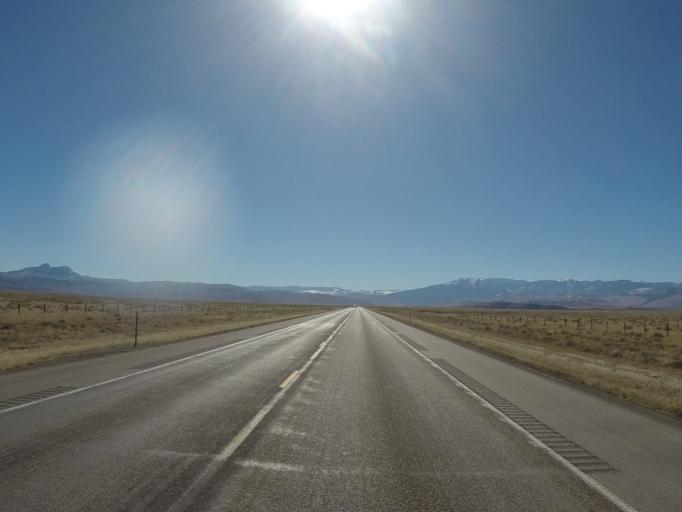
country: US
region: Wyoming
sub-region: Park County
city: Cody
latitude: 44.8391
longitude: -109.1514
